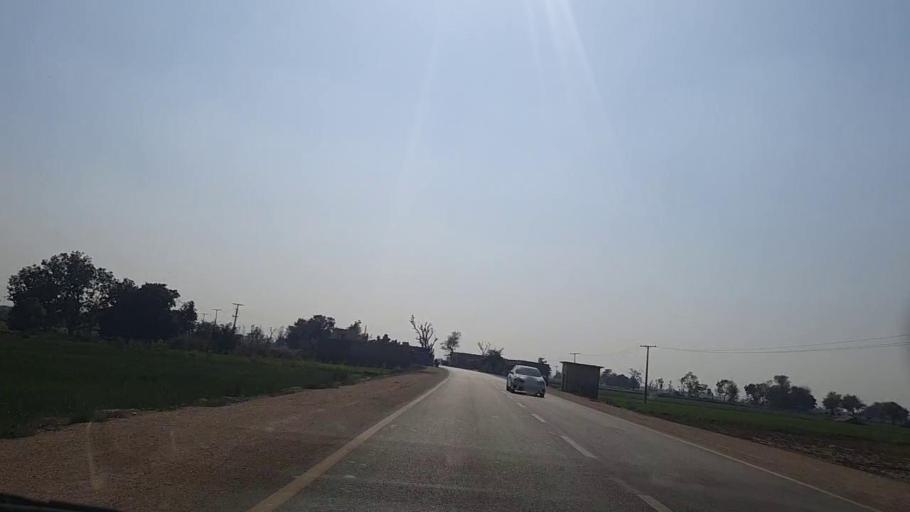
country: PK
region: Sindh
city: Sakrand
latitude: 26.0300
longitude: 68.3995
